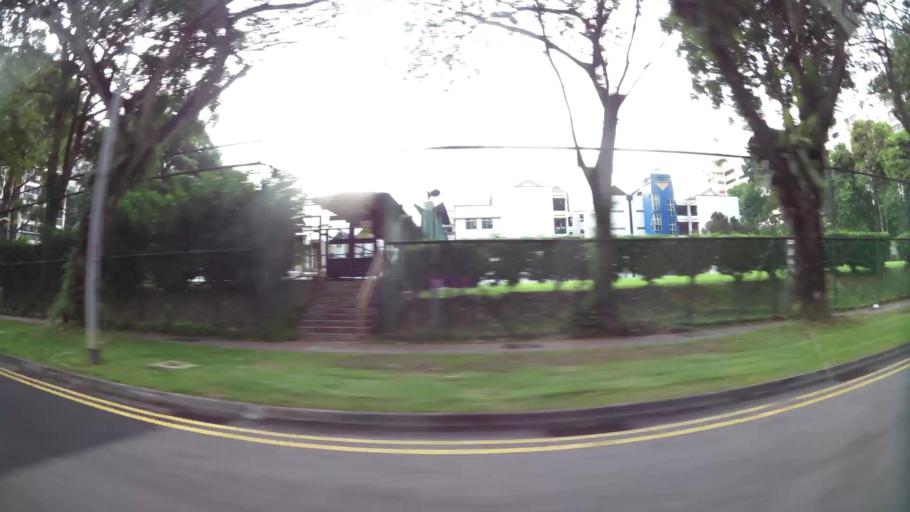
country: MY
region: Johor
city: Kampung Pasir Gudang Baru
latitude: 1.4277
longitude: 103.8494
